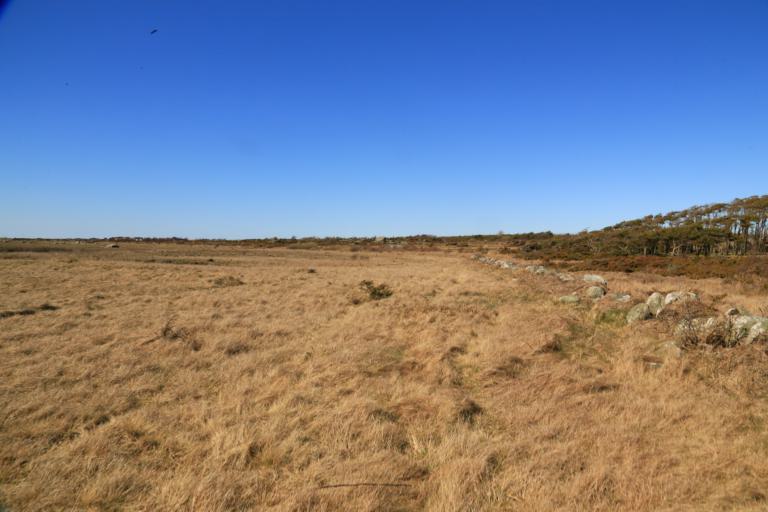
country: SE
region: Halland
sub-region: Varbergs Kommun
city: Traslovslage
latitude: 57.0417
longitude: 12.2899
